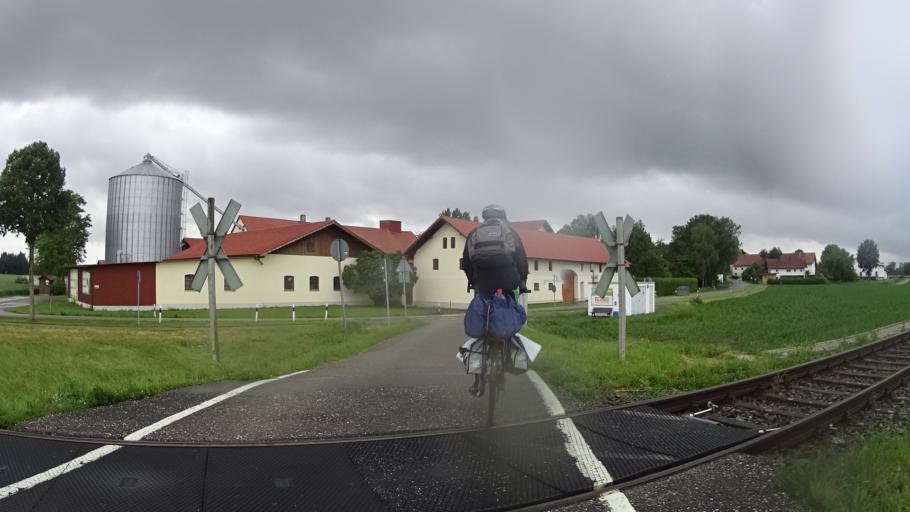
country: DE
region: Bavaria
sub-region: Lower Bavaria
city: Pocking
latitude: 48.4067
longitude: 13.2935
